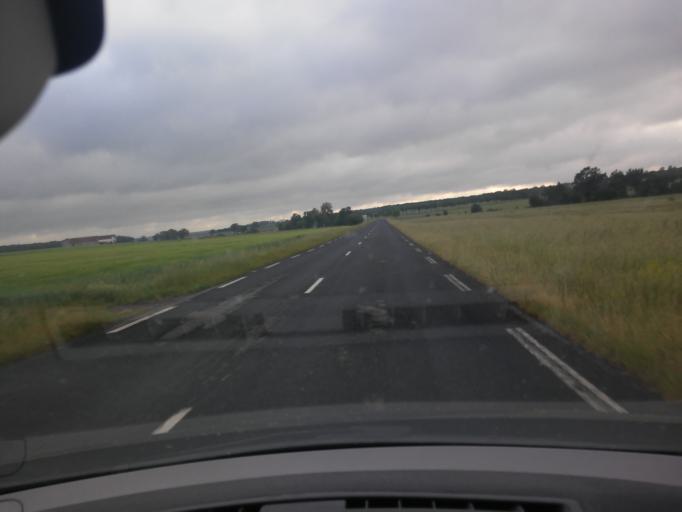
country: FR
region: Lorraine
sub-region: Departement de la Meuse
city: Vigneulles-les-Hattonchatel
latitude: 48.9887
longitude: 5.7941
